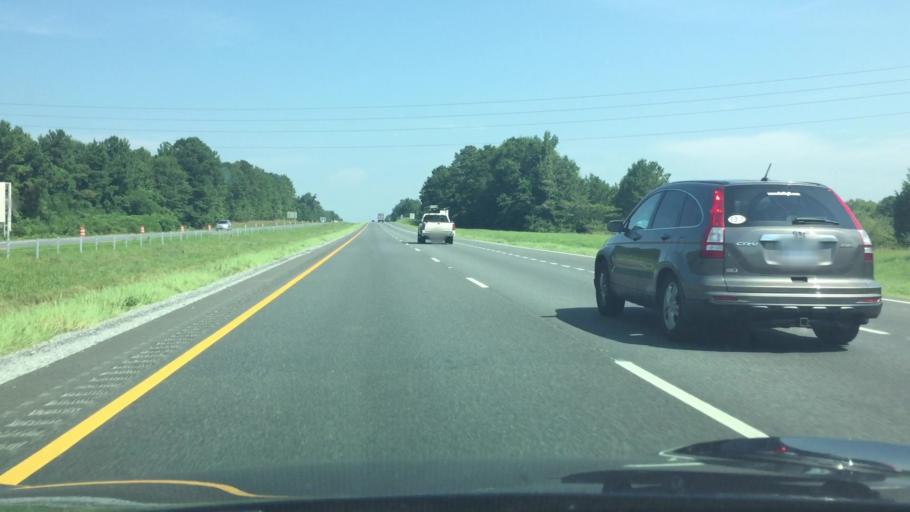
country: US
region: Alabama
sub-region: Chilton County
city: Clanton
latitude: 32.8063
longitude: -86.5817
